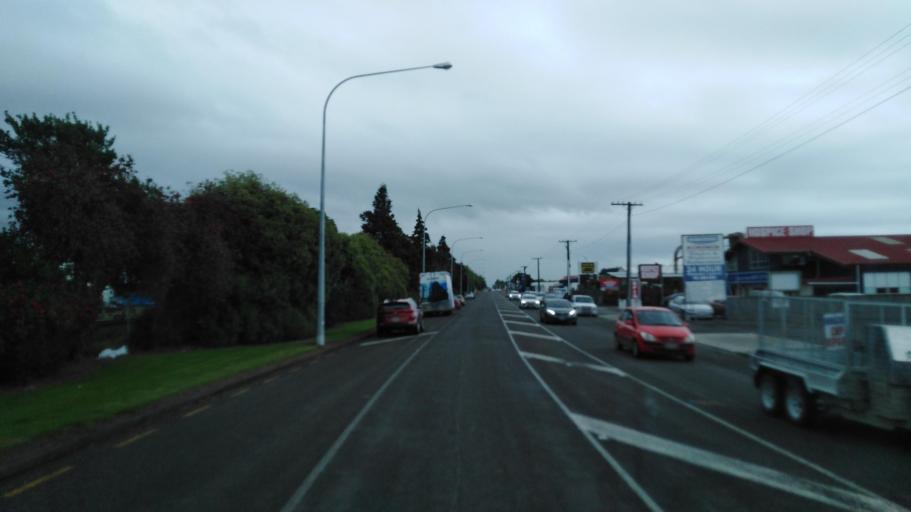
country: NZ
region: Manawatu-Wanganui
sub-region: Horowhenua District
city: Levin
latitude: -40.6334
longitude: 175.2755
